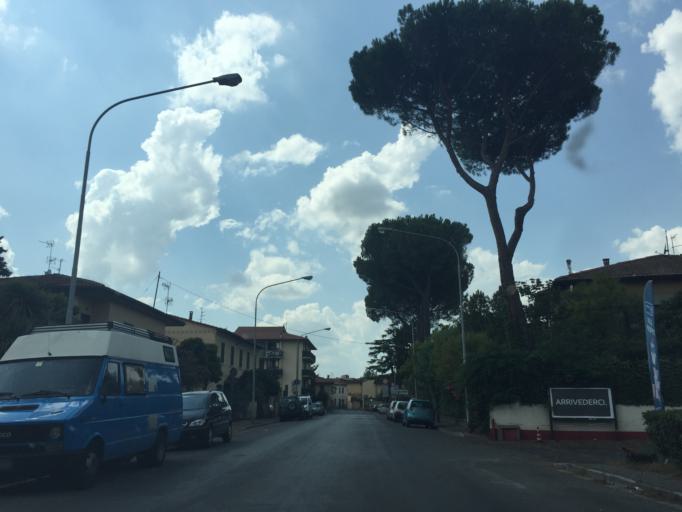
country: IT
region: Tuscany
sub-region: Province of Florence
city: San Donnino
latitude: 43.7940
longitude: 11.1563
